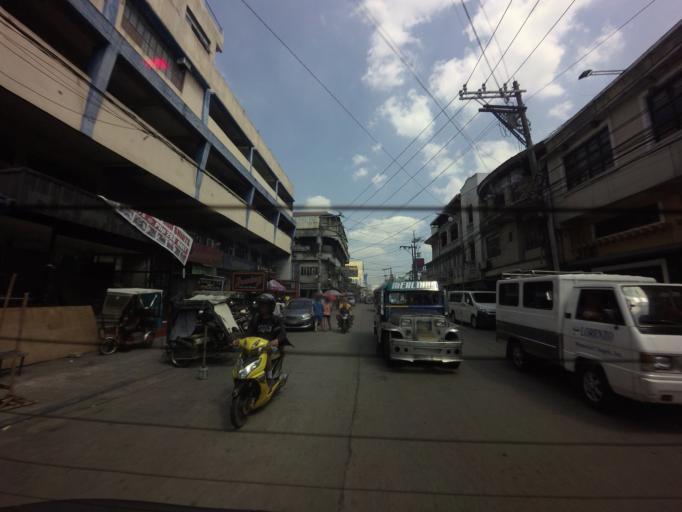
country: PH
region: Metro Manila
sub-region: City of Manila
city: Manila
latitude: 14.6152
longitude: 120.9697
